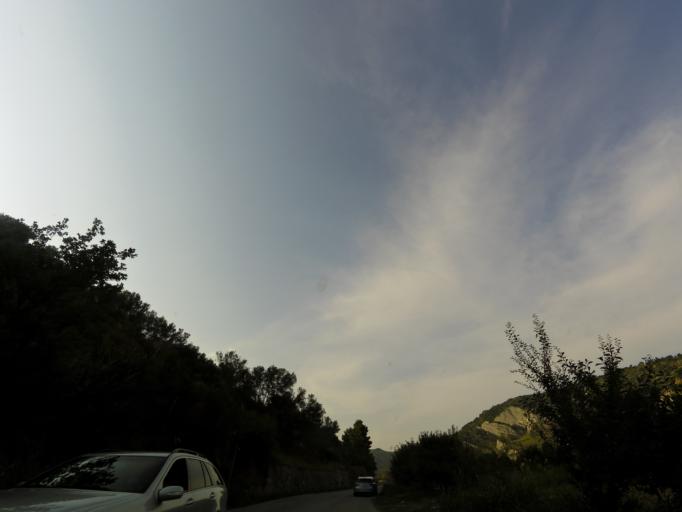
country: IT
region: Calabria
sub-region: Provincia di Reggio Calabria
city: Stilo
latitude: 38.4687
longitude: 16.4849
